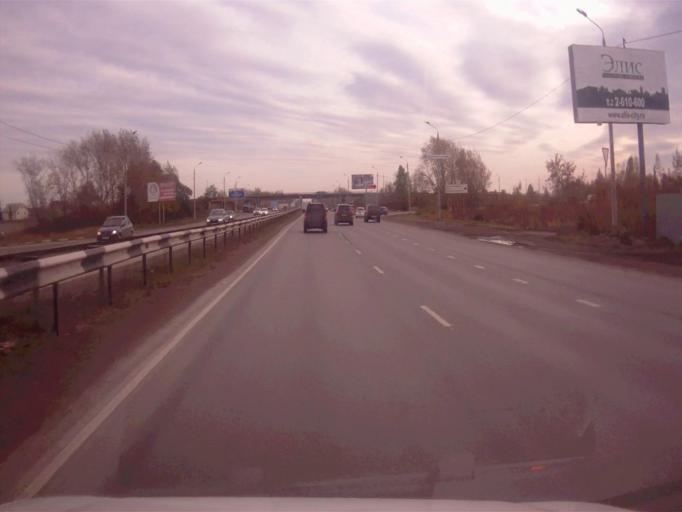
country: RU
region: Chelyabinsk
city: Novosineglazovskiy
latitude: 55.0643
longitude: 61.3976
